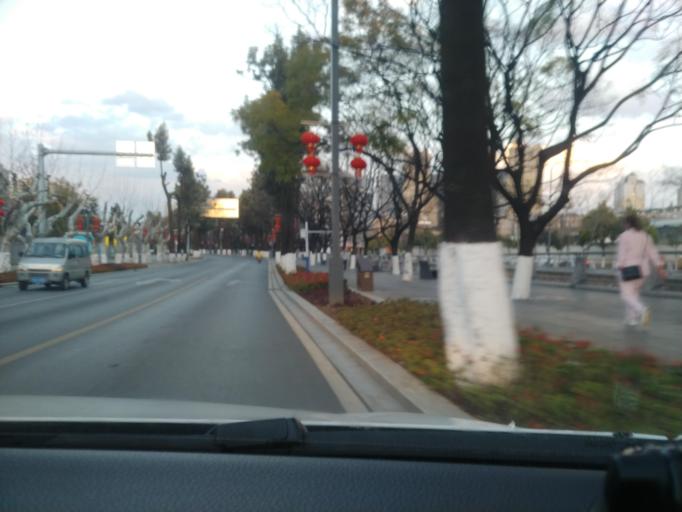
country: CN
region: Yunnan
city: Kunming
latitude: 25.0356
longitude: 102.6810
